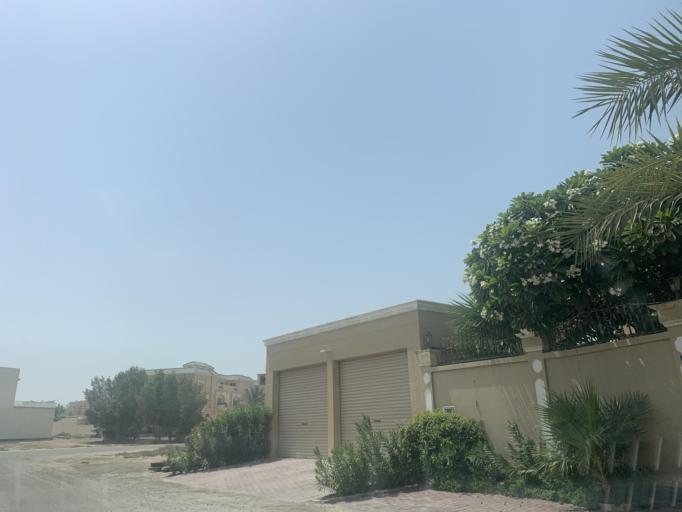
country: BH
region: Manama
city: Jidd Hafs
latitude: 26.2006
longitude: 50.5048
